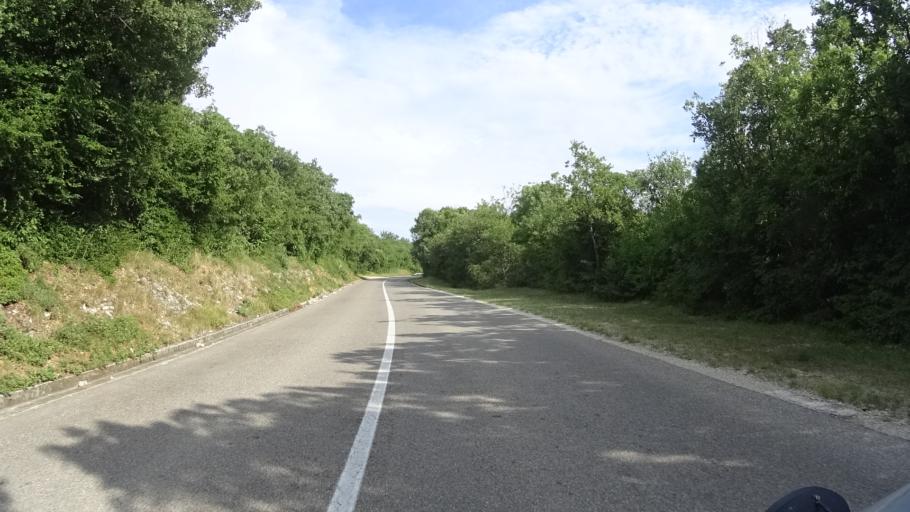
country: HR
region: Istarska
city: Rasa
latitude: 45.0248
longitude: 14.0855
